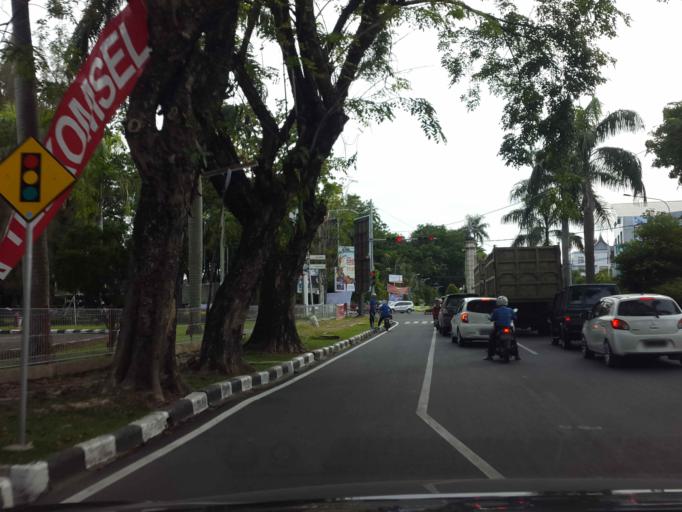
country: ID
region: West Sumatra
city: Padang
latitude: -0.9259
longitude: 100.3621
